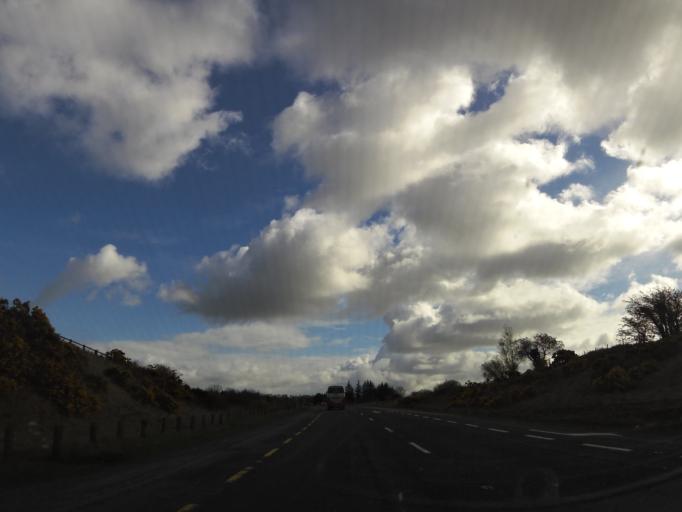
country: IE
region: Connaught
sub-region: Maigh Eo
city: Ballyhaunis
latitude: 53.8300
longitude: -8.8693
